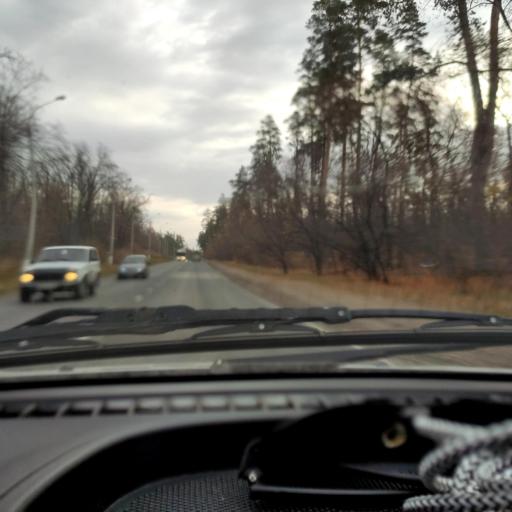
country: RU
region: Samara
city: Tol'yatti
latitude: 53.4933
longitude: 49.2964
